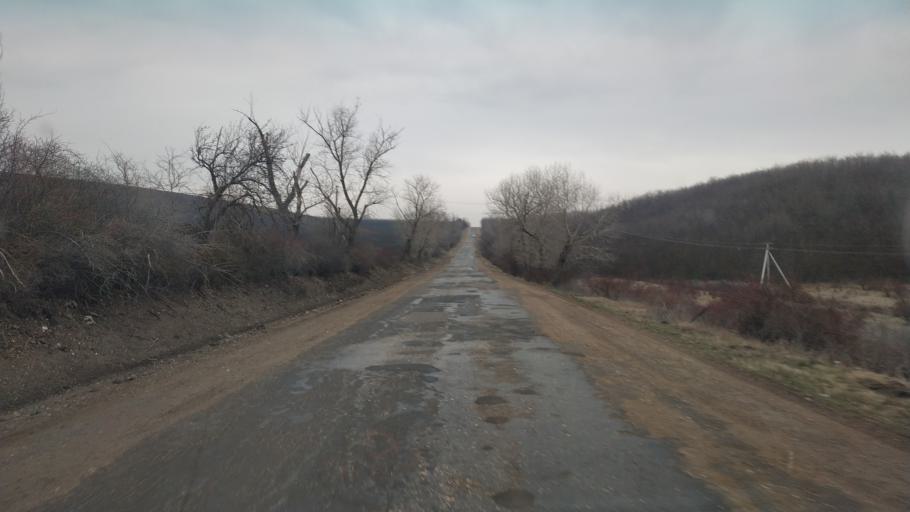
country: MD
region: Chisinau
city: Singera
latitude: 46.8469
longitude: 28.9895
